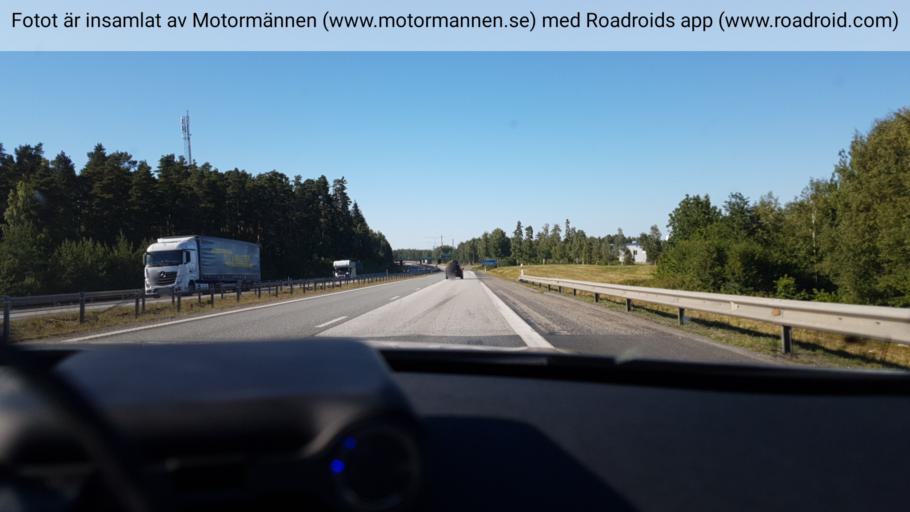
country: SE
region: Joenkoeping
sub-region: Jonkopings Kommun
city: Odensjo
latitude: 57.7414
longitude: 14.1589
